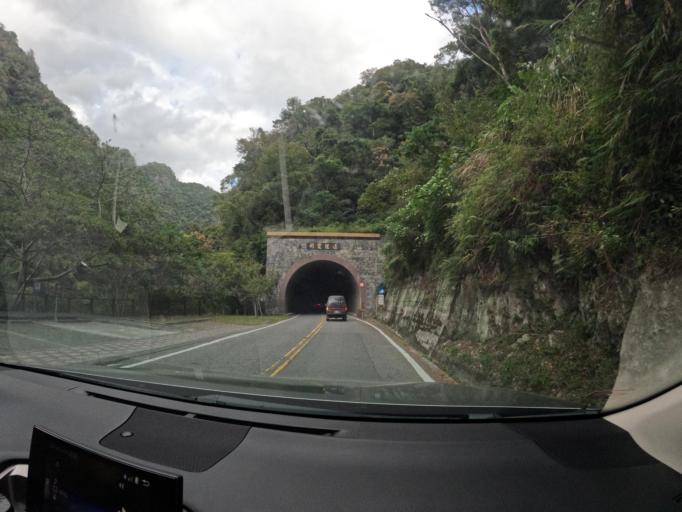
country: TW
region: Taiwan
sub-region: Taitung
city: Taitung
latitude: 23.1387
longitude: 121.1039
